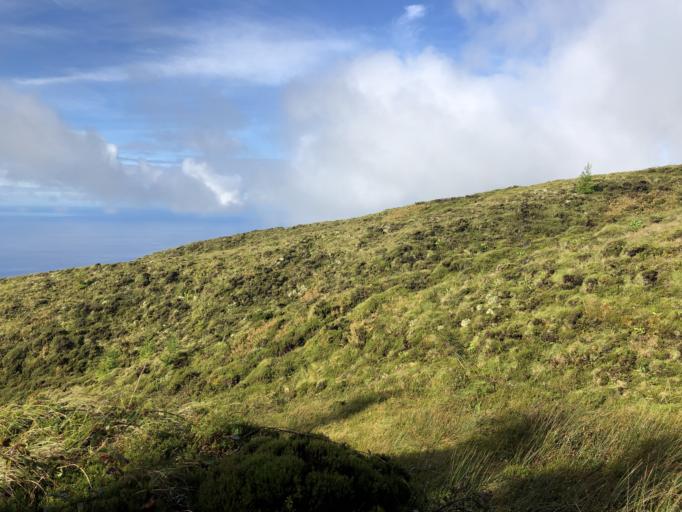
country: PT
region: Azores
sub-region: Ponta Delgada
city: Arrifes
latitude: 37.8385
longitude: -25.7629
